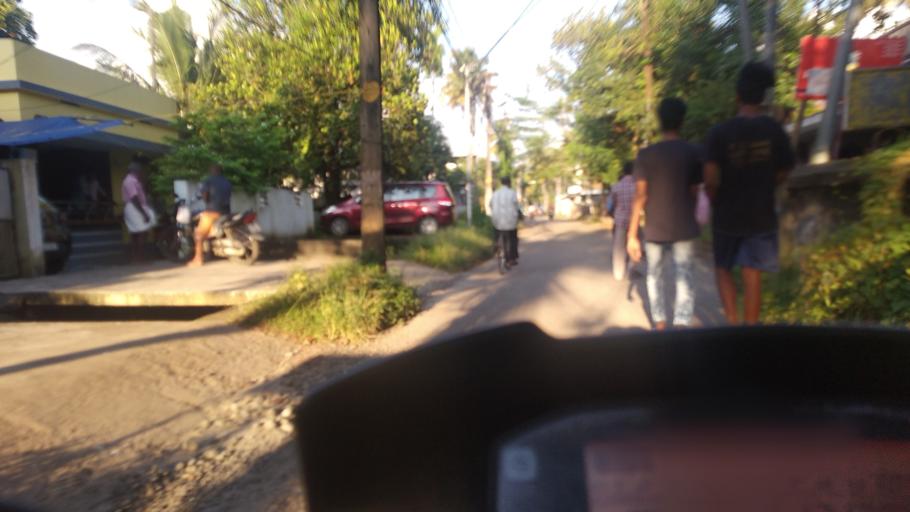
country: IN
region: Kerala
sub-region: Ernakulam
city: Cochin
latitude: 9.9448
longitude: 76.3255
